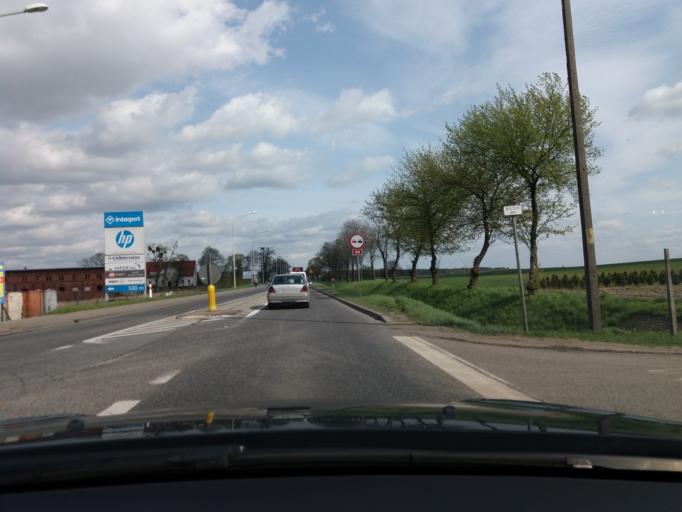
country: PL
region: Lower Silesian Voivodeship
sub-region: Powiat sredzki
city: Miekinia
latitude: 51.1587
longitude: 16.7450
